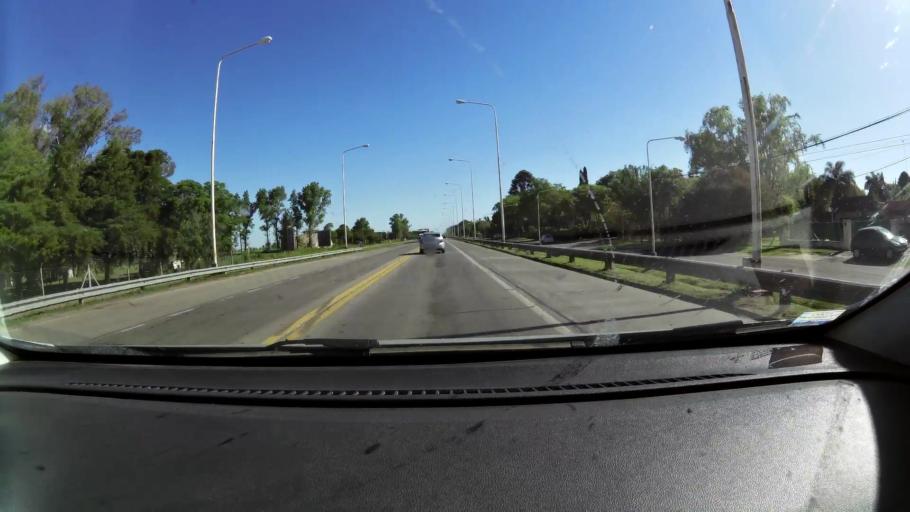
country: AR
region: Santa Fe
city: Rafaela
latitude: -31.2797
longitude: -61.5122
